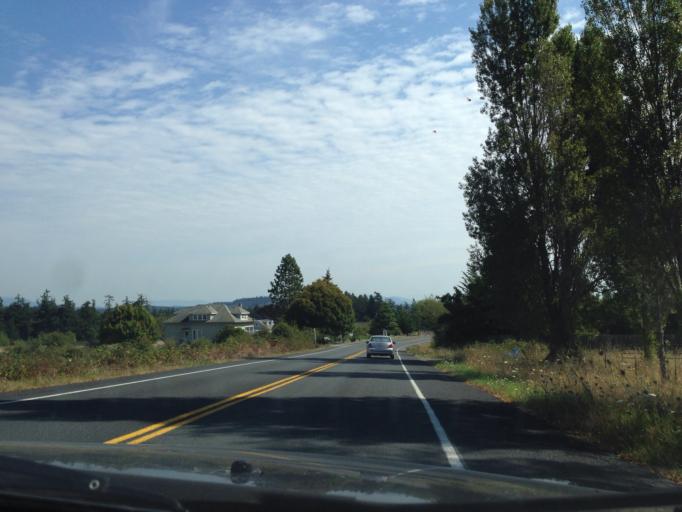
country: US
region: Washington
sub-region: San Juan County
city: Friday Harbor
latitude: 48.5106
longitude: -123.0351
